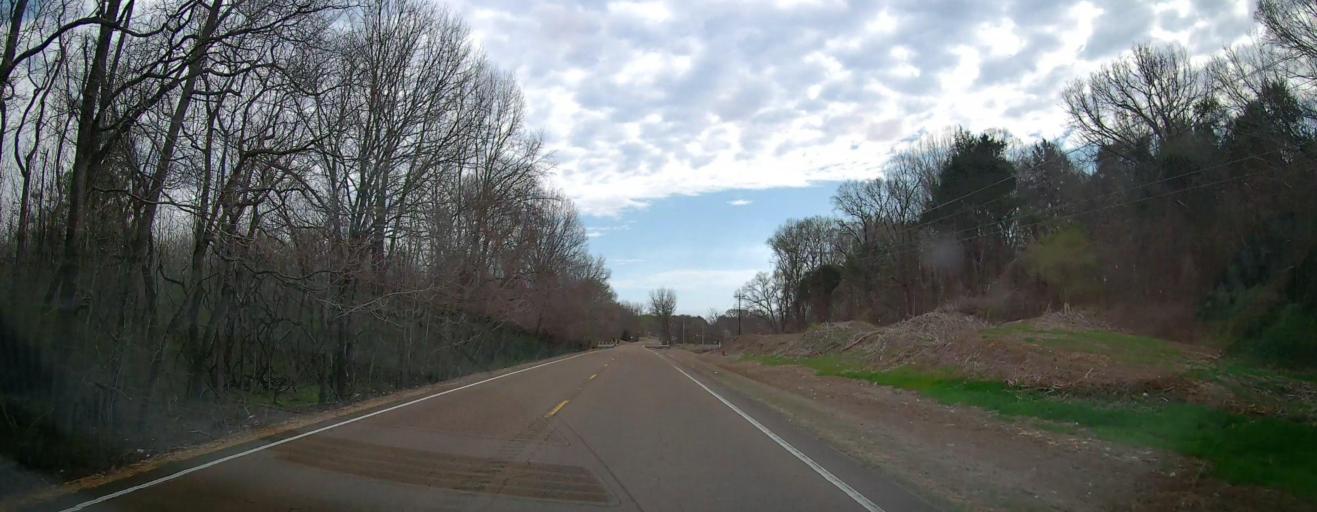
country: US
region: Mississippi
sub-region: Marshall County
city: Byhalia
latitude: 34.8480
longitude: -89.6246
